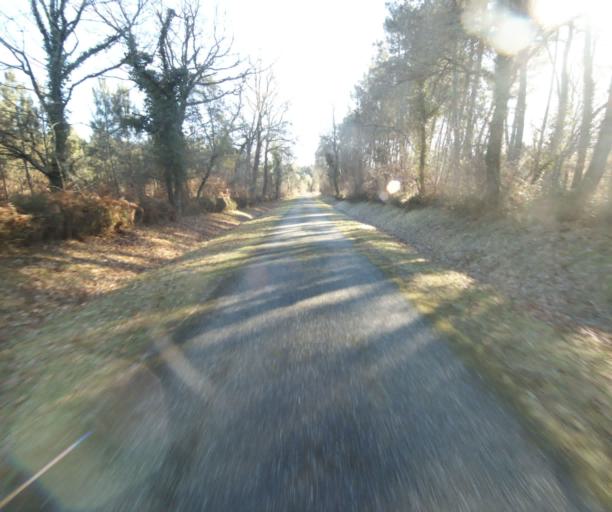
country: FR
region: Aquitaine
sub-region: Departement des Landes
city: Gabarret
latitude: 44.0992
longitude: 0.0868
